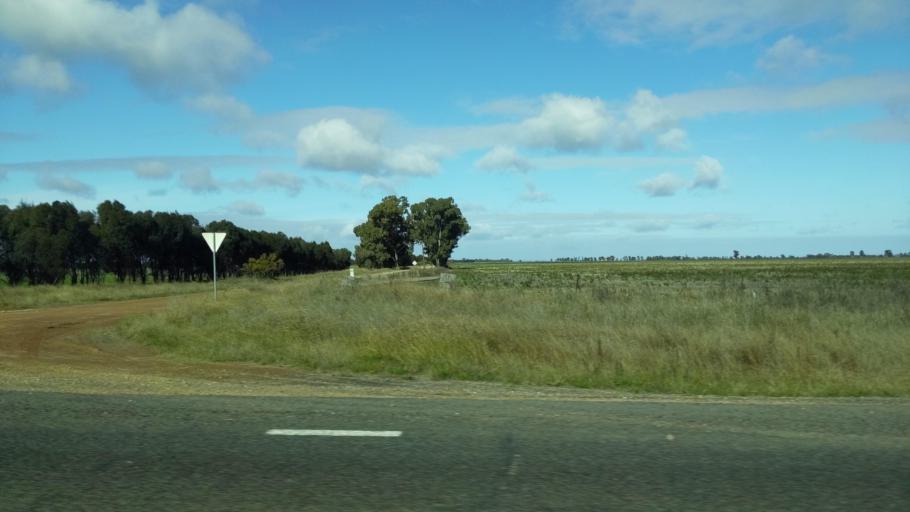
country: AU
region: New South Wales
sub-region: Coolamon
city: Coolamon
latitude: -34.7617
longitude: 146.8905
